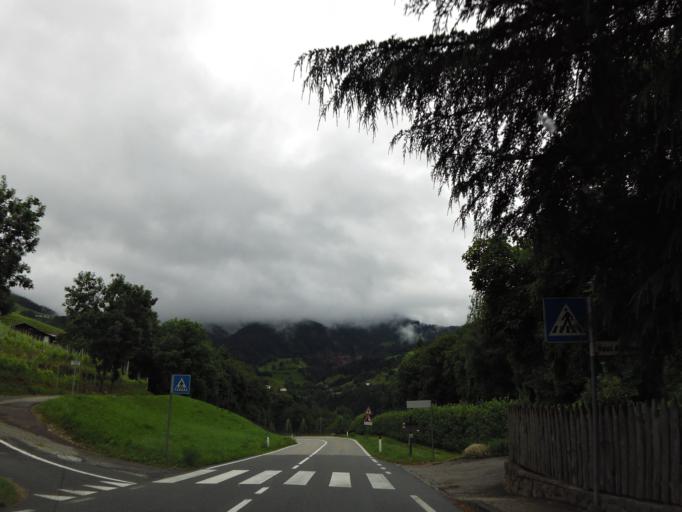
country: IT
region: Trentino-Alto Adige
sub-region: Bolzano
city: Fie Allo Sciliar
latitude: 46.5153
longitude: 11.5059
